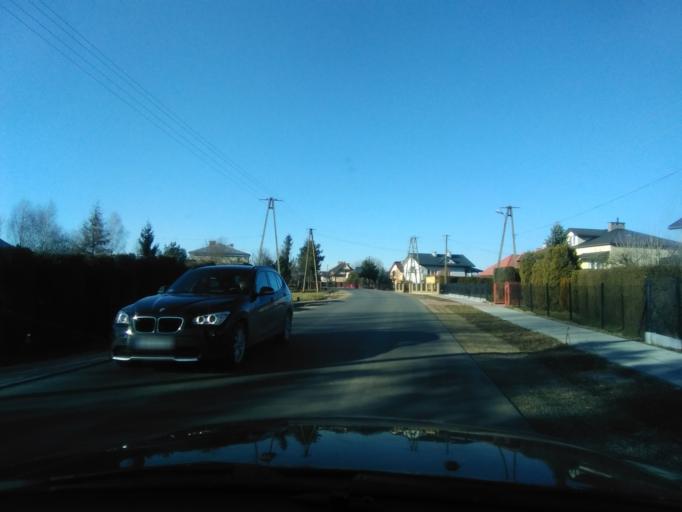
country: PL
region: Subcarpathian Voivodeship
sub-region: Powiat krosnienski
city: Rymanow
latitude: 49.6079
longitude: 21.8976
